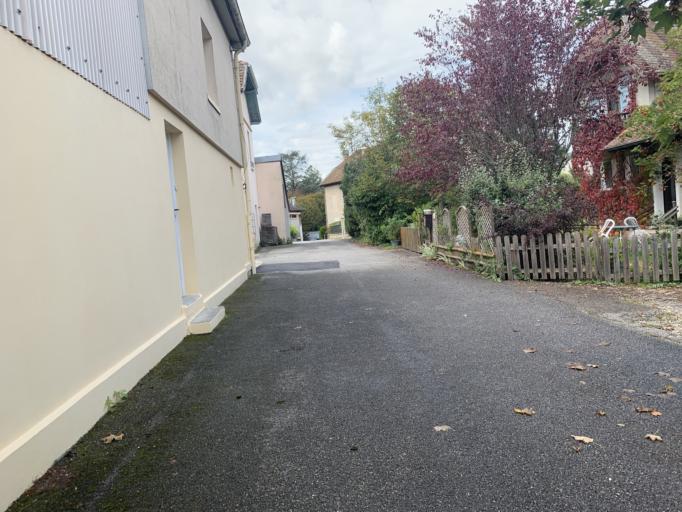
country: FR
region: Rhone-Alpes
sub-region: Departement de l'Ain
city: Belley
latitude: 45.7600
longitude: 5.6937
